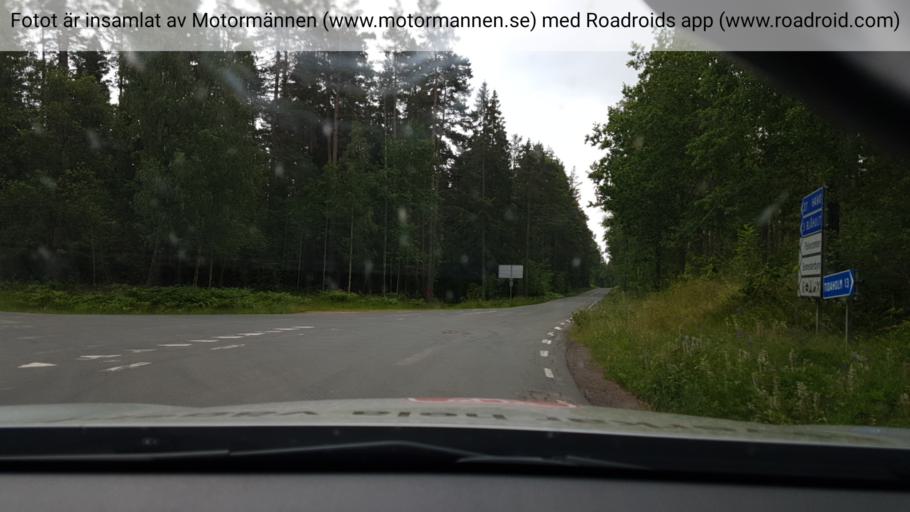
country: SE
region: Vaestra Goetaland
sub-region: Tidaholms Kommun
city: Tidaholm
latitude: 58.1034
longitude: 14.0768
